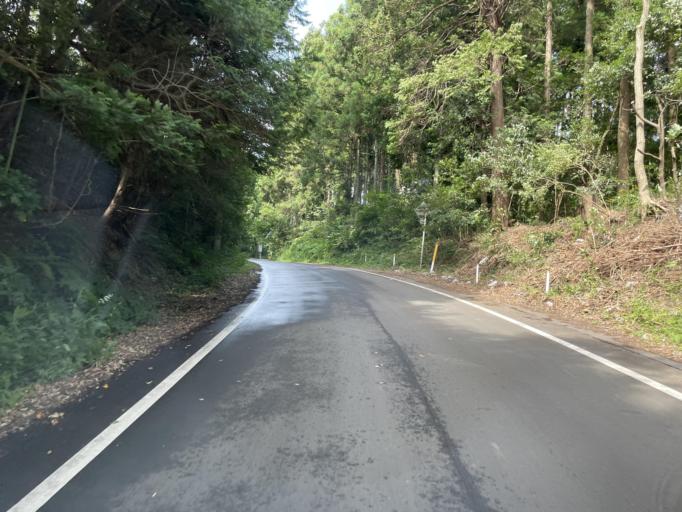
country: JP
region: Chiba
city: Sawara
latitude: 35.8003
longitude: 140.4677
